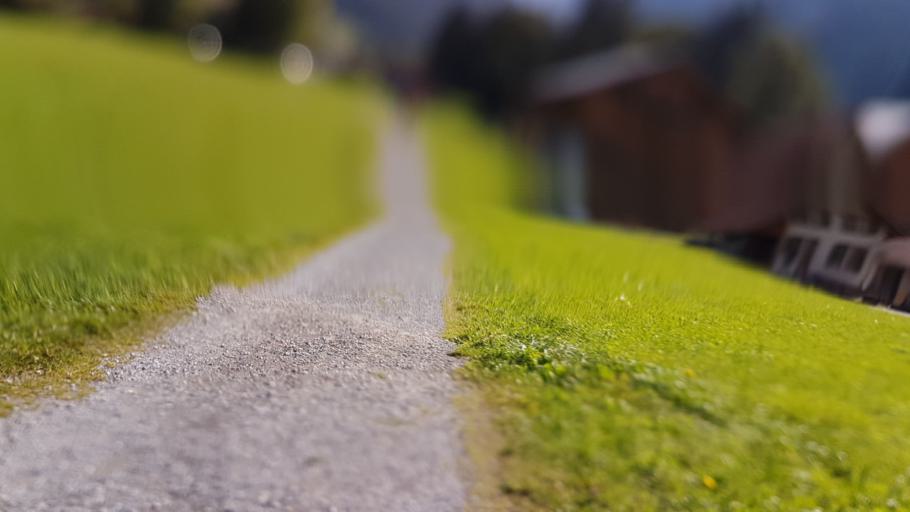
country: CH
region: Bern
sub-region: Frutigen-Niedersimmental District
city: Kandersteg
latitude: 46.4950
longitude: 7.6767
